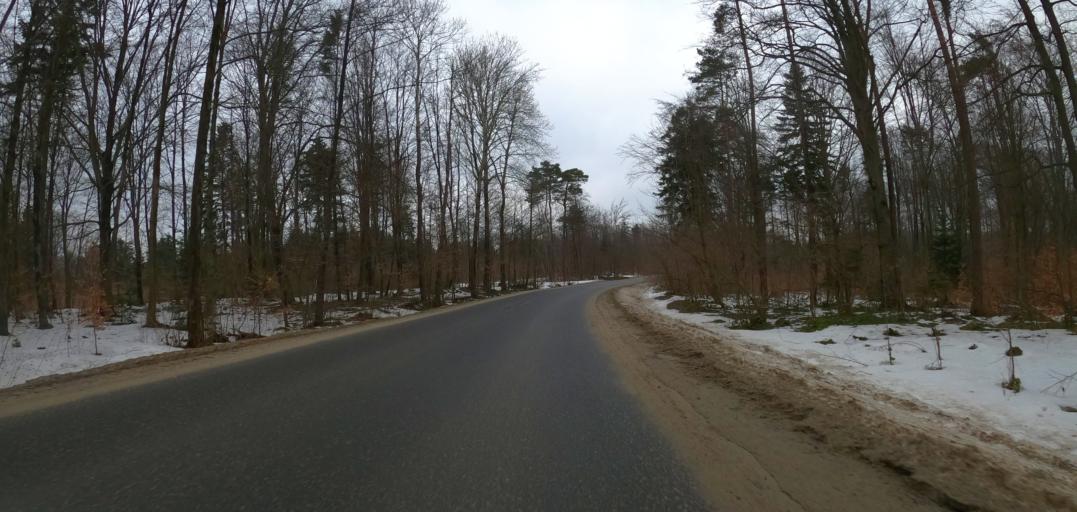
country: PL
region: Subcarpathian Voivodeship
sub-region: Powiat debicki
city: Debica
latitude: 49.9790
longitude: 21.4090
